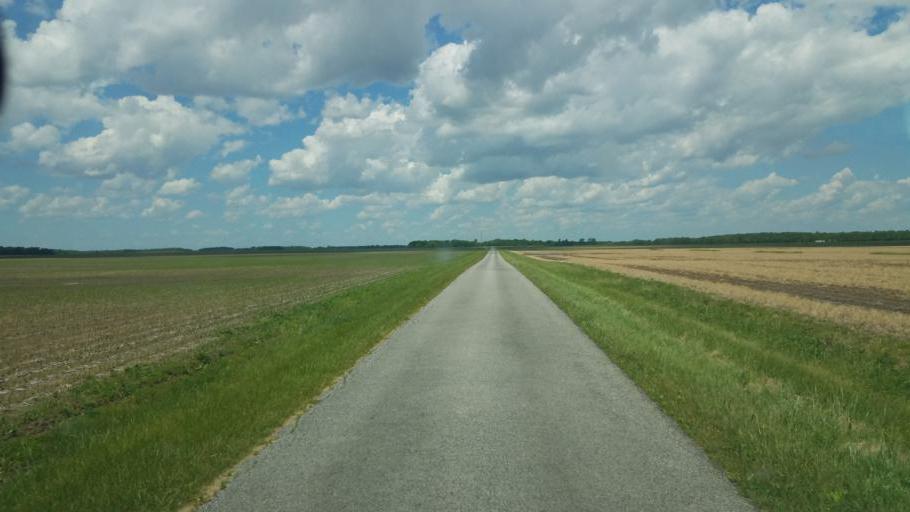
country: US
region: Ohio
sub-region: Wyandot County
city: Upper Sandusky
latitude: 40.7501
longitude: -83.2408
